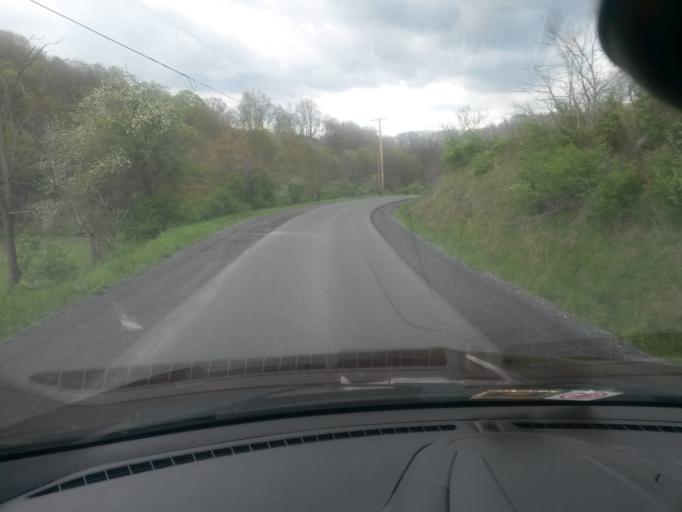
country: US
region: West Virginia
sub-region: Greenbrier County
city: Lewisburg
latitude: 37.9367
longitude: -80.4253
